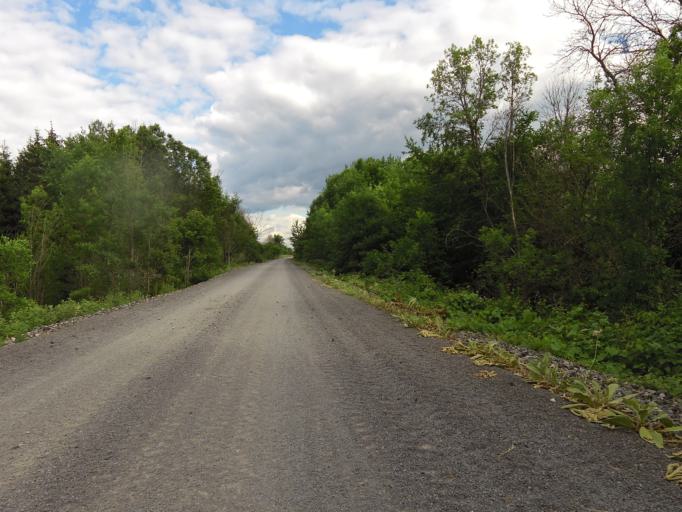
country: CA
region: Ontario
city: Carleton Place
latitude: 45.2828
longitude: -76.2464
